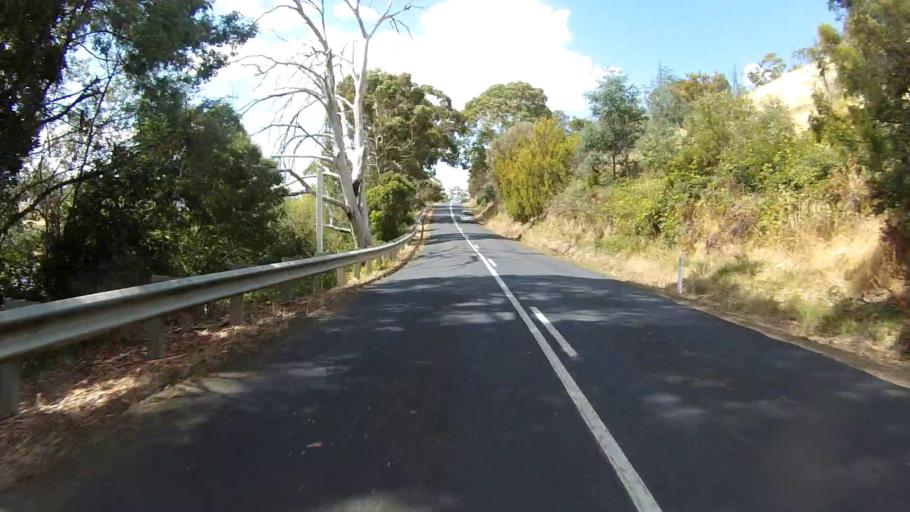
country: AU
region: Tasmania
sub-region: Derwent Valley
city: New Norfolk
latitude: -42.7320
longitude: 146.9047
